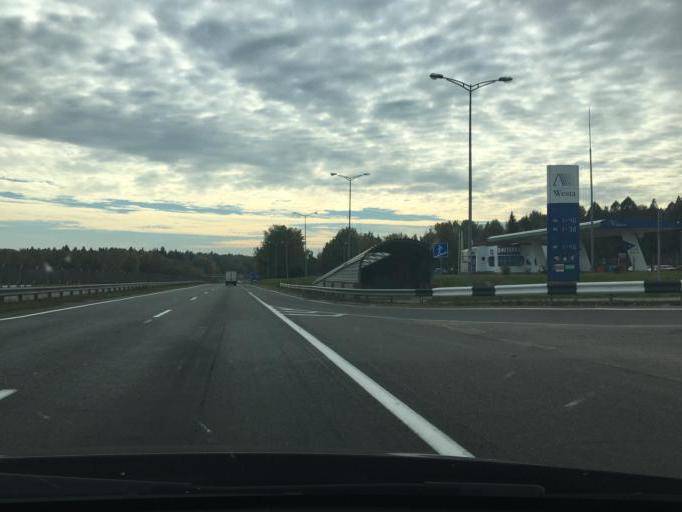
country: BY
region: Minsk
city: Enyerhyetykaw
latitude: 53.5959
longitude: 27.0423
